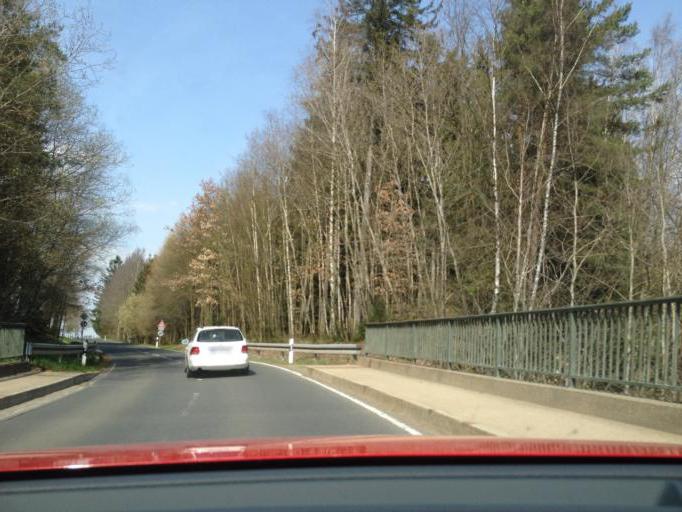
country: DE
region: Bavaria
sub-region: Upper Franconia
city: Arzberg
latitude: 50.0402
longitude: 12.1661
